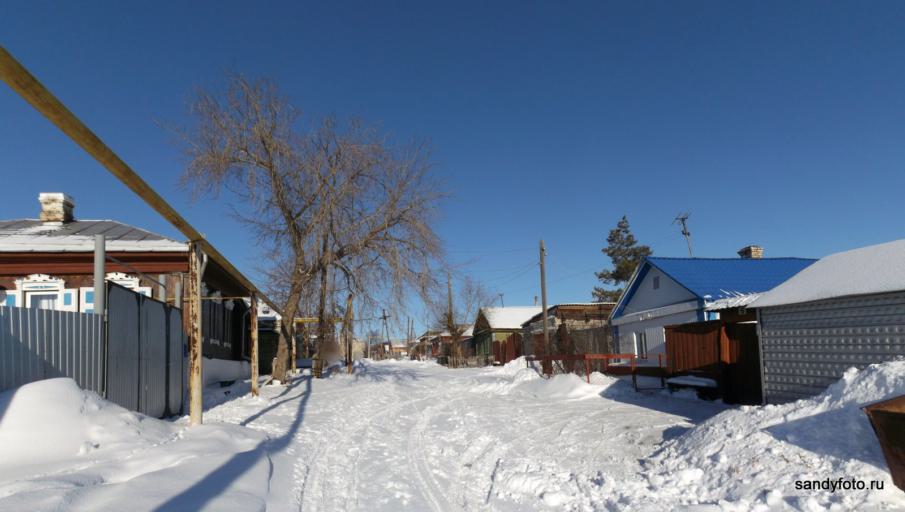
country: RU
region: Chelyabinsk
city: Troitsk
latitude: 54.1002
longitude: 61.5597
